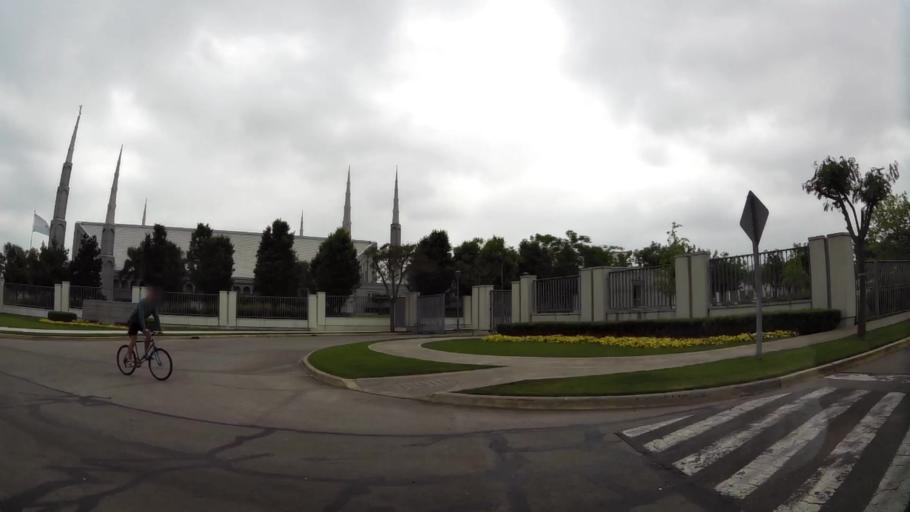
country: AR
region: Buenos Aires F.D.
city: Villa Lugano
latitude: -34.7287
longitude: -58.5176
